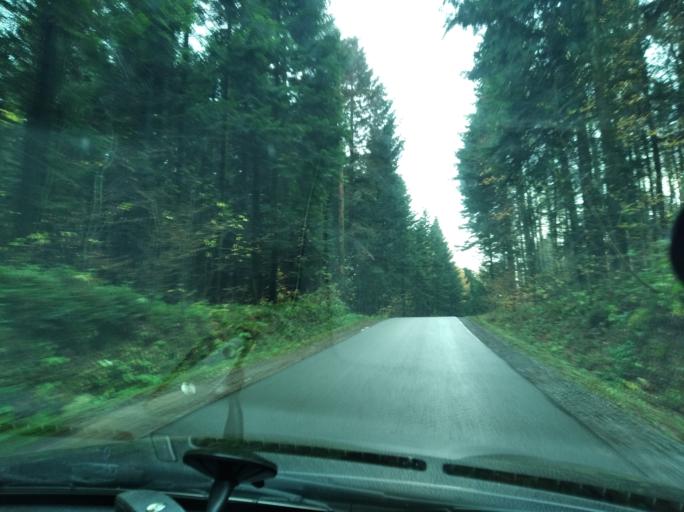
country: PL
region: Subcarpathian Voivodeship
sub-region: Powiat strzyzowski
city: Strzyzow
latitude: 49.9041
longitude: 21.7845
